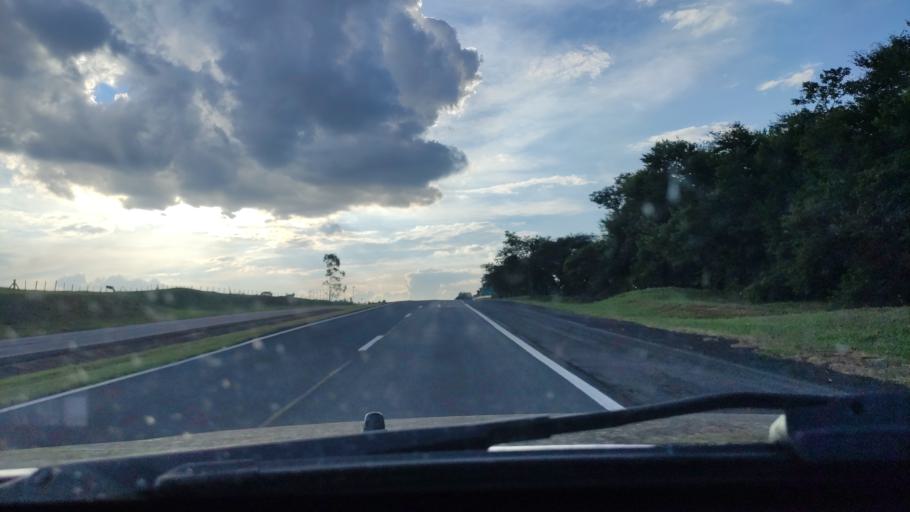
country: BR
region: Sao Paulo
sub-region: Rancharia
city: Rancharia
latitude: -22.4852
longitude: -50.9226
